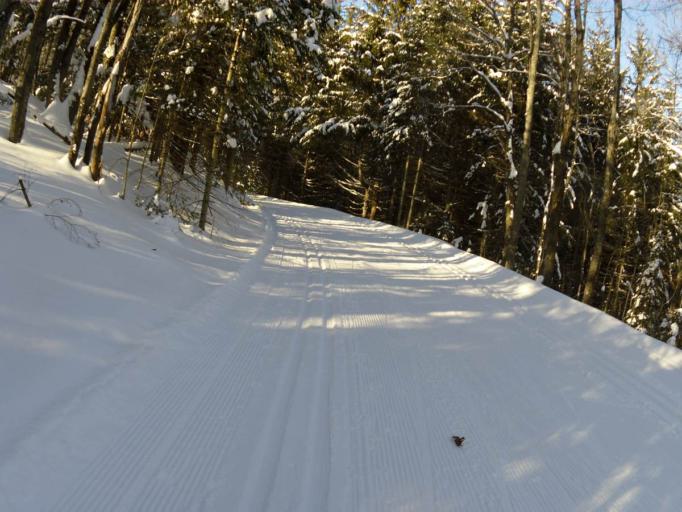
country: CA
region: Quebec
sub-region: Outaouais
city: Wakefield
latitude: 45.6321
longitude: -75.9433
